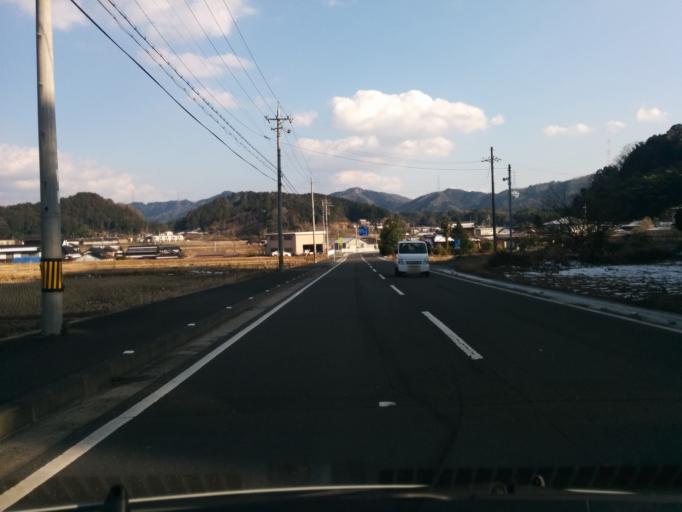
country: JP
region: Kyoto
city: Ayabe
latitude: 35.3602
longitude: 135.2175
